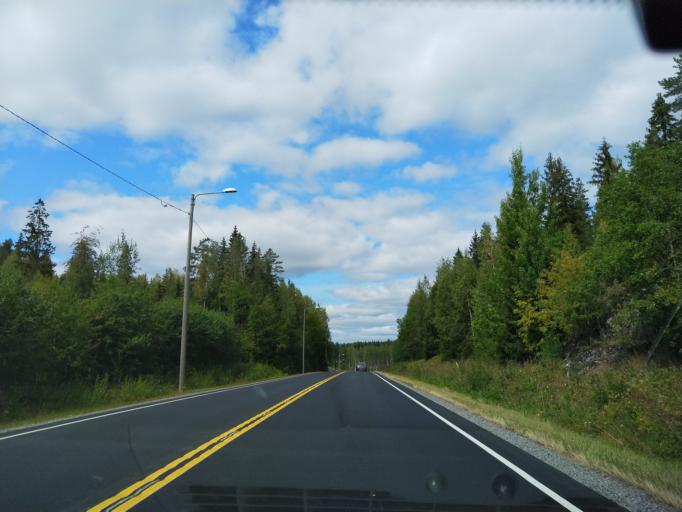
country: FI
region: Haeme
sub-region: Riihimaeki
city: Loppi
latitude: 60.7162
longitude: 24.4670
